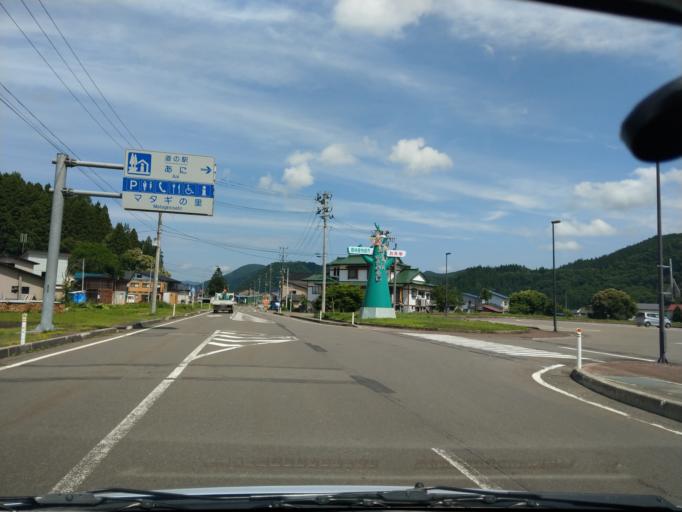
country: JP
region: Akita
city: Kakunodatemachi
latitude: 39.9011
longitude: 140.4568
